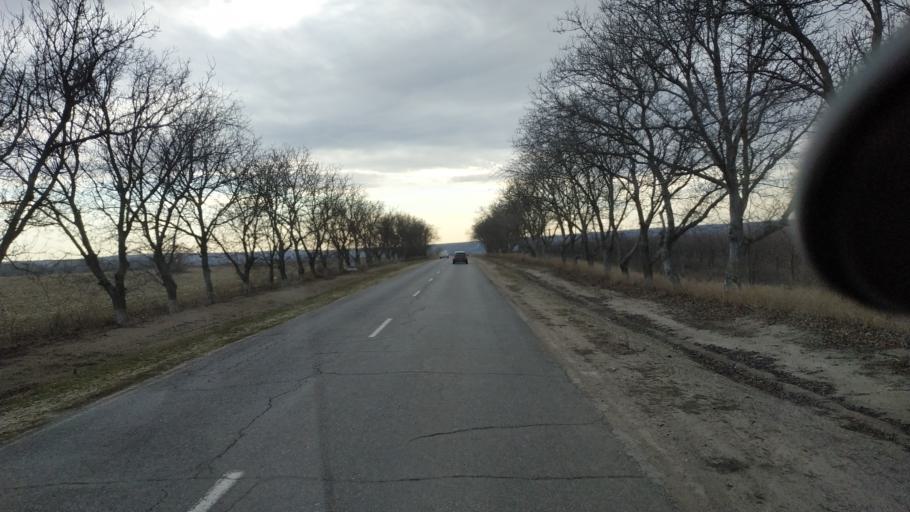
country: MD
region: Chisinau
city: Vadul lui Voda
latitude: 47.1559
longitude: 29.1064
